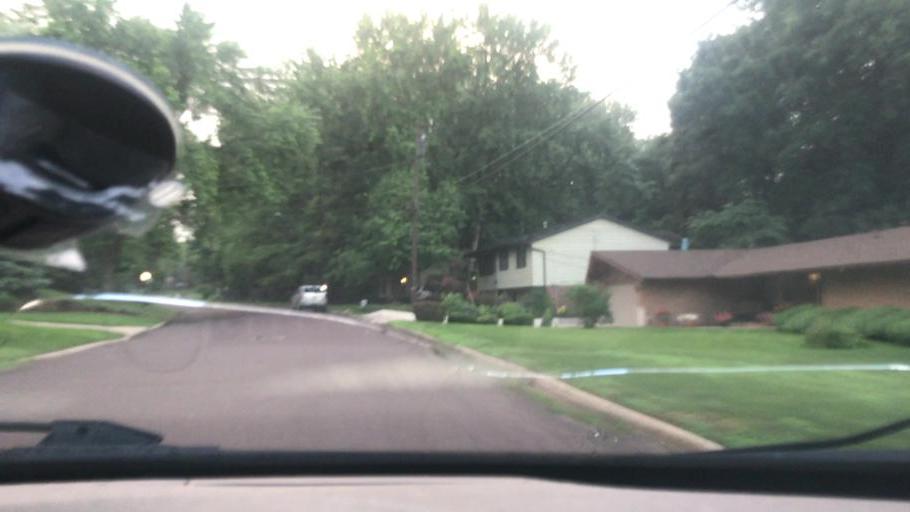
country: US
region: Illinois
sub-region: Tazewell County
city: Pekin
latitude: 40.5541
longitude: -89.6149
